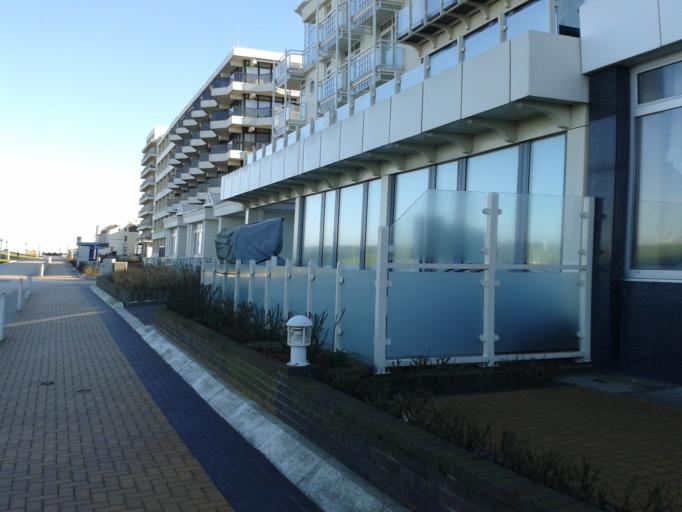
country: DE
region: Lower Saxony
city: Norderney
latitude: 53.7089
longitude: 7.1409
